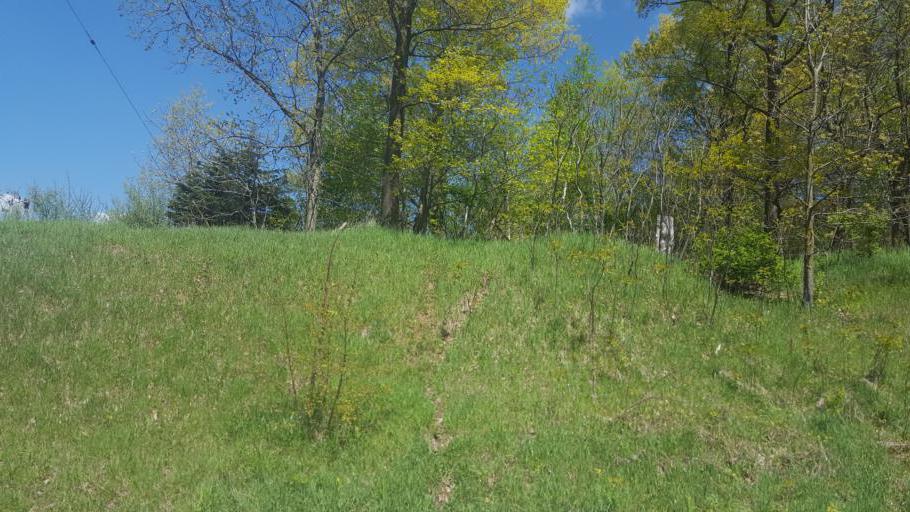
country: US
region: Wisconsin
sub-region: Vernon County
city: Hillsboro
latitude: 43.6424
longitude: -90.3673
